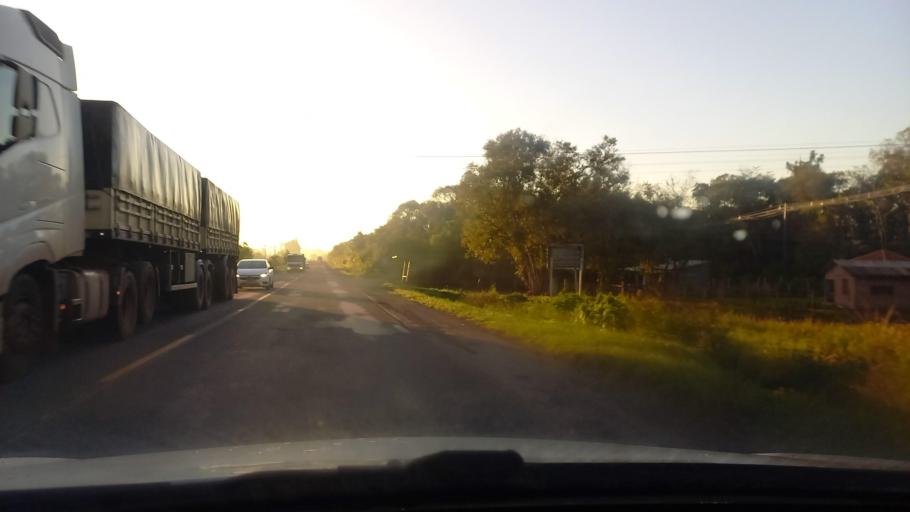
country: BR
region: Rio Grande do Sul
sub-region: Candelaria
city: Candelaria
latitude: -29.6808
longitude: -52.8339
